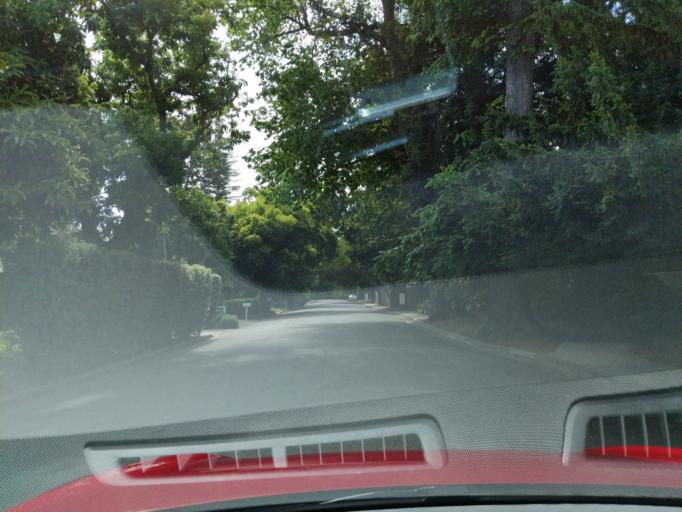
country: US
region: California
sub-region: San Mateo County
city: Menlo Park
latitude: 37.4420
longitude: -122.1790
